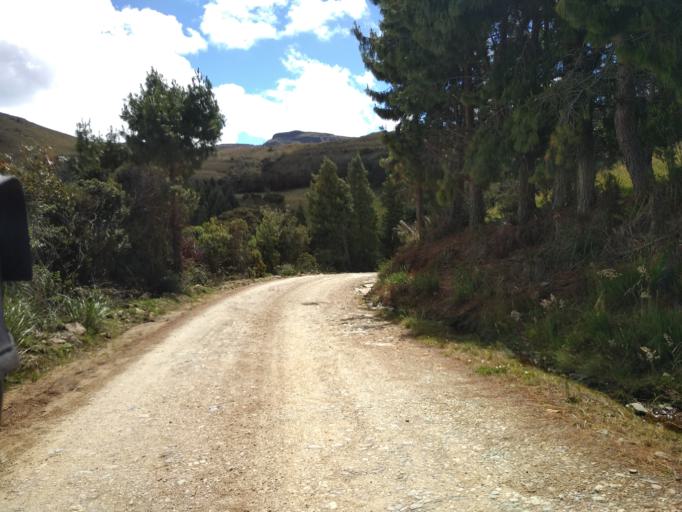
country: CO
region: Boyaca
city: Duitama
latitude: 5.9302
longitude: -73.0883
